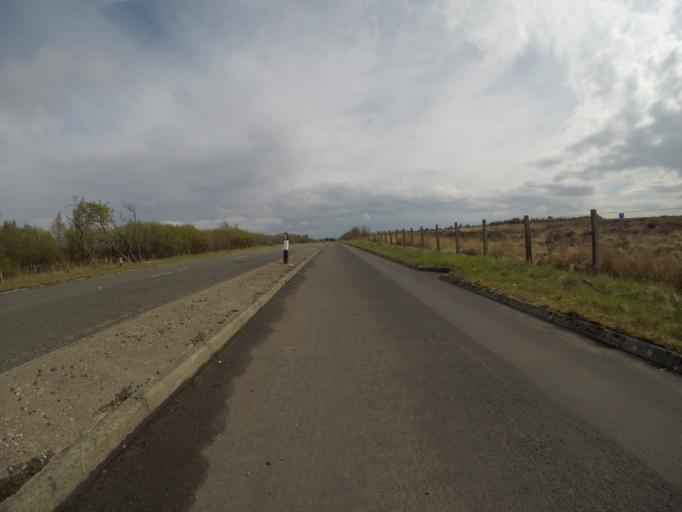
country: GB
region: Scotland
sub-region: East Renfrewshire
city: Neilston
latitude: 55.7020
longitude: -4.3960
